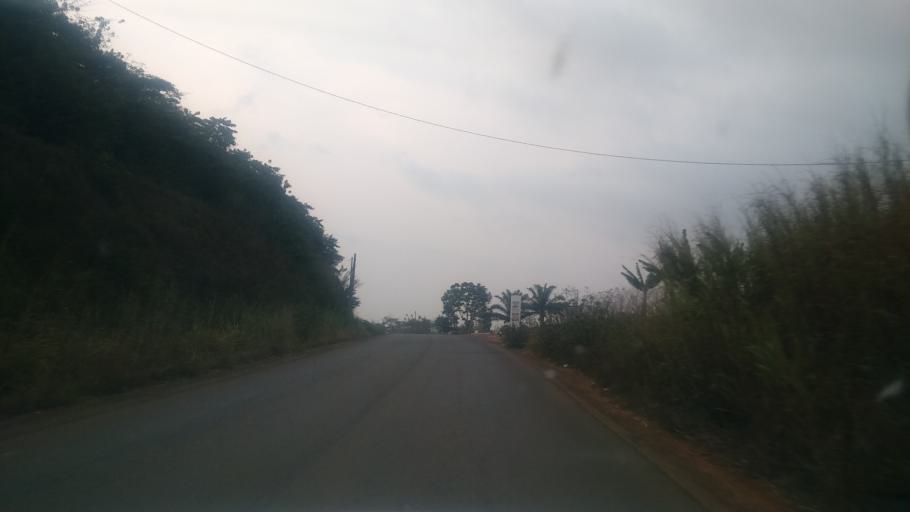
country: CM
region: West
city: Bana
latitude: 5.1489
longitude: 10.2755
